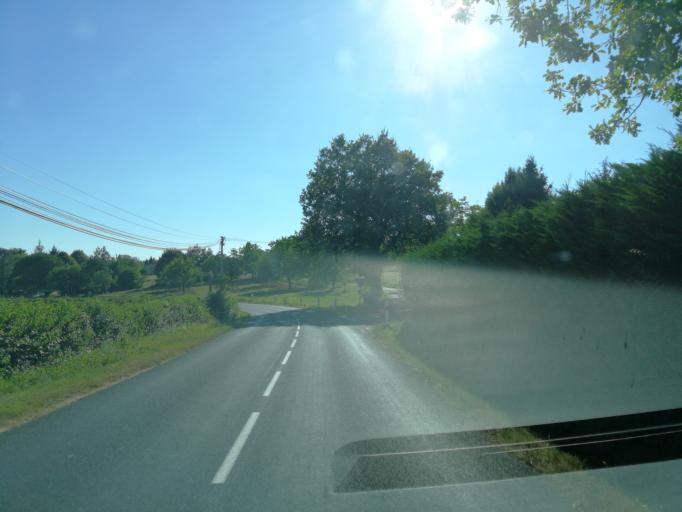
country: FR
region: Midi-Pyrenees
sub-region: Departement du Lot
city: Gourdon
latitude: 44.7187
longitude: 1.3594
